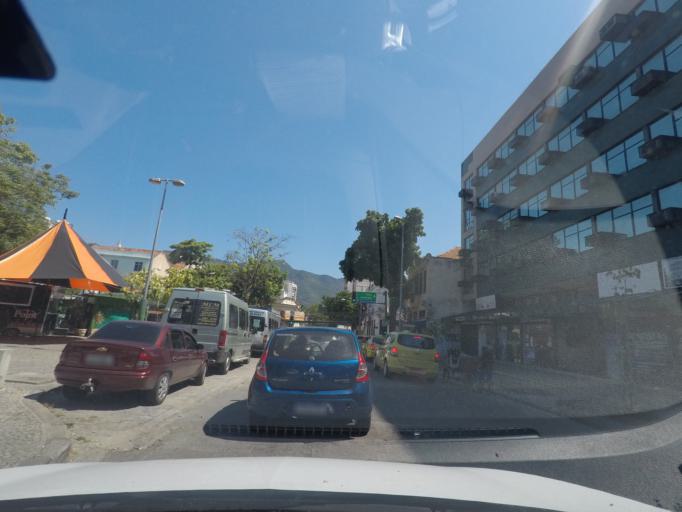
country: BR
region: Rio de Janeiro
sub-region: Rio De Janeiro
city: Rio de Janeiro
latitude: -22.9170
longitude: -43.2513
